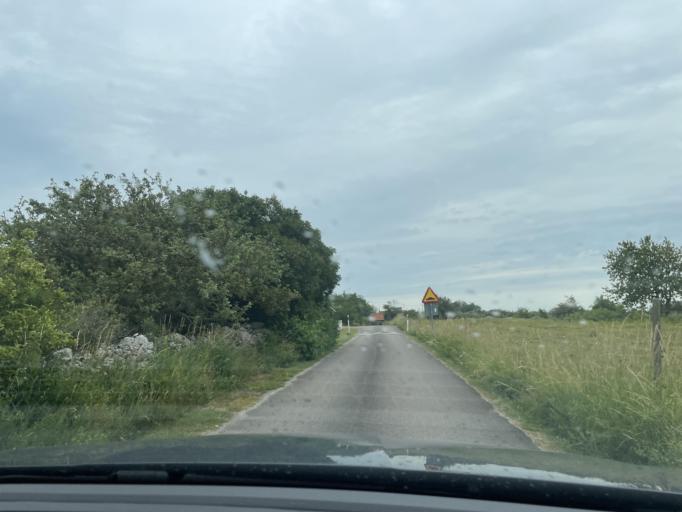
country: SE
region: Skane
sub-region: Bromolla Kommun
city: Bromoella
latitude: 56.0001
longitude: 14.4439
